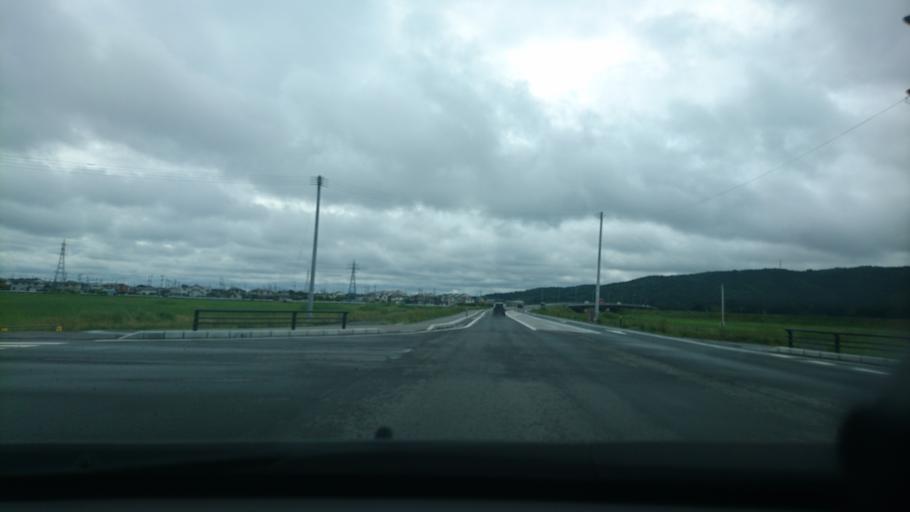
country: JP
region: Miyagi
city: Ishinomaki
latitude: 38.4491
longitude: 141.3428
